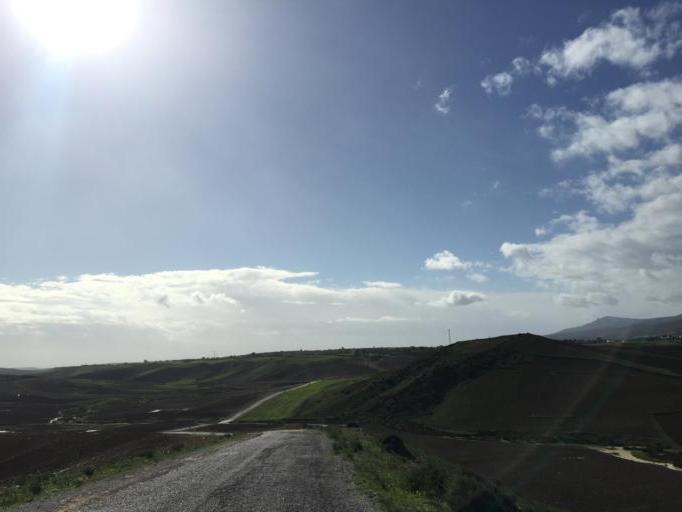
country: TN
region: Nabul
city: El Mida
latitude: 36.8625
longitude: 10.8608
